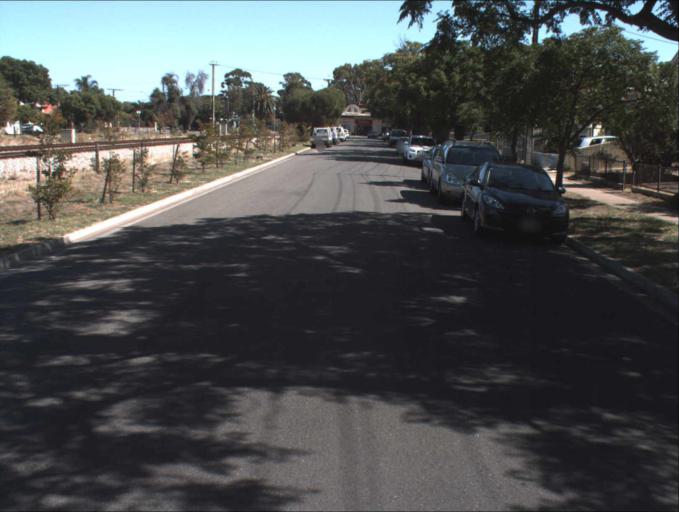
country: AU
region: South Australia
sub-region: Port Adelaide Enfield
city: Alberton
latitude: -34.8604
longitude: 138.5205
